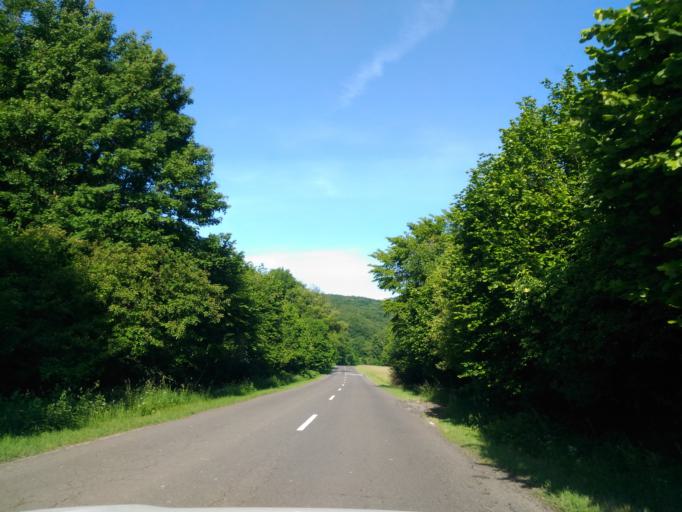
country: HU
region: Baranya
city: Hosszuheteny
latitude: 46.1952
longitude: 18.3135
